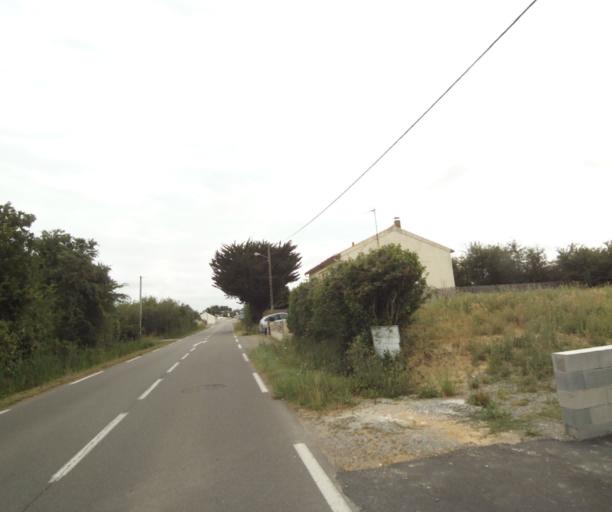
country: FR
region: Pays de la Loire
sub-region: Departement de la Vendee
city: Chateau-d'Olonne
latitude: 46.4799
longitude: -1.7176
